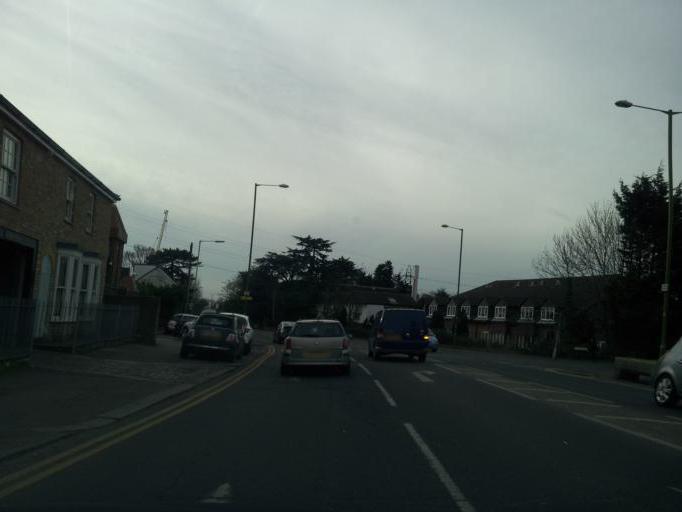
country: GB
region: England
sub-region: Hertfordshire
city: Bushey
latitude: 51.6370
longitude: -0.3468
